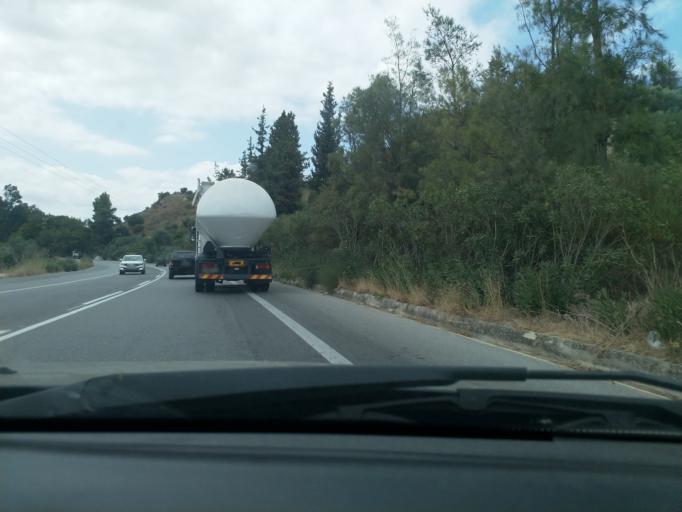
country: GR
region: Crete
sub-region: Nomos Chanias
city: Georgioupolis
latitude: 35.3777
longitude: 24.2065
